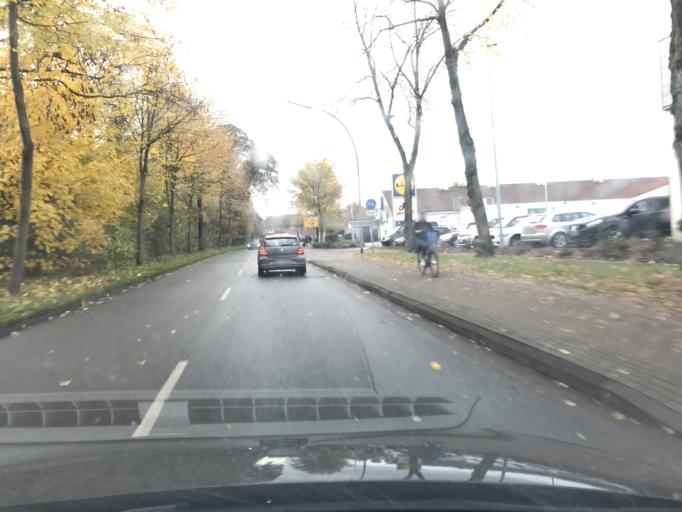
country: DE
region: North Rhine-Westphalia
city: Oelde
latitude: 51.8311
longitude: 8.1534
